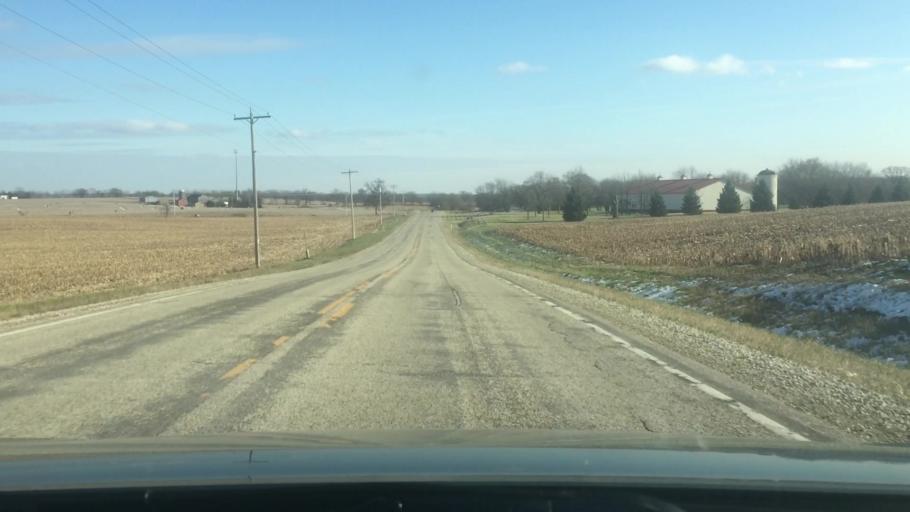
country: US
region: Wisconsin
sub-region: Jefferson County
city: Palmyra
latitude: 42.9292
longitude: -88.5658
